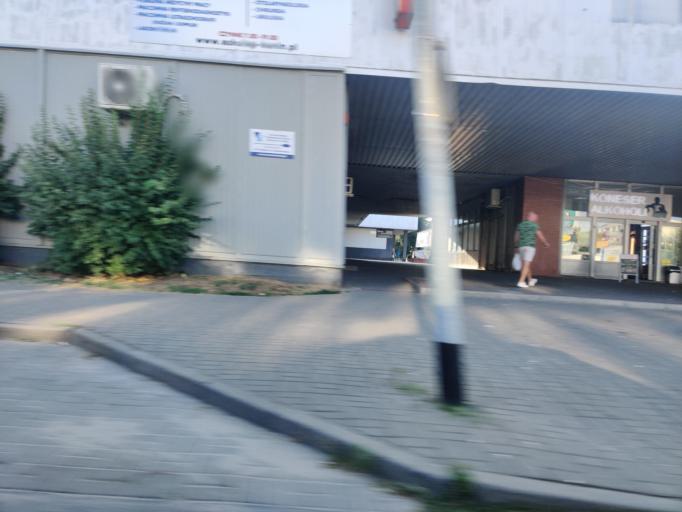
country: PL
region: Greater Poland Voivodeship
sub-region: Konin
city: Konin
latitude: 52.2341
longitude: 18.2604
